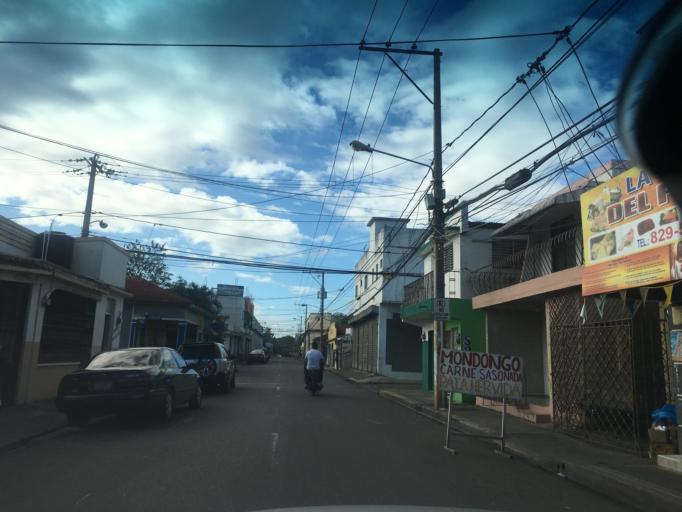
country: DO
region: Duarte
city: San Francisco de Macoris
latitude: 19.2973
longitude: -70.2598
